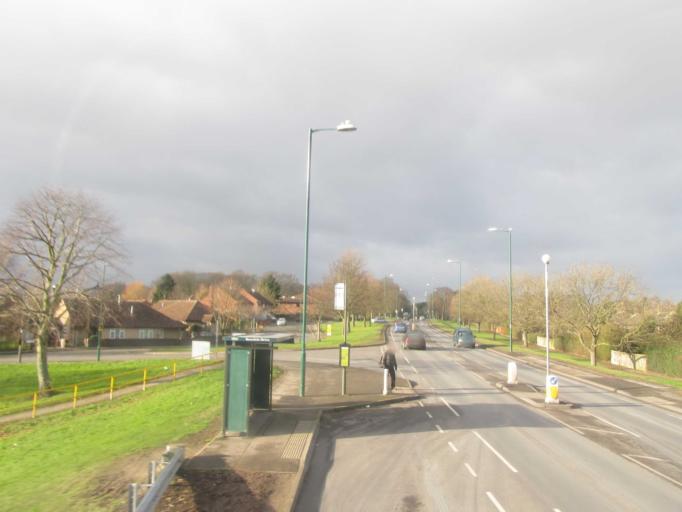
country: GB
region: England
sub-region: Nottinghamshire
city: Kimberley
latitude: 52.9517
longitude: -1.2403
